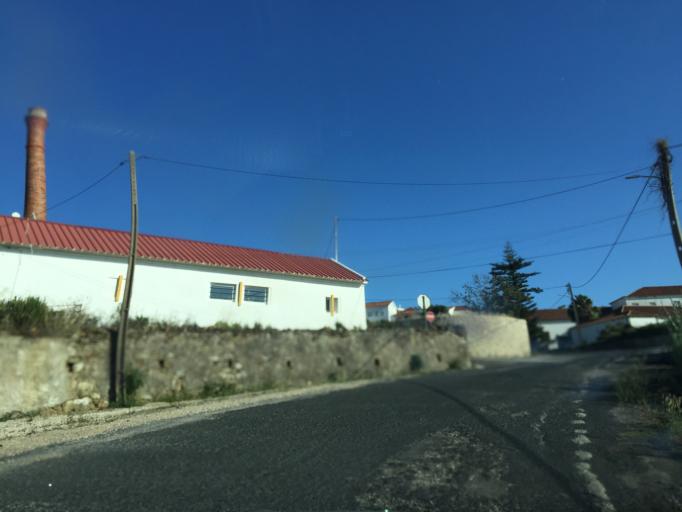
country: PT
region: Lisbon
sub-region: Torres Vedras
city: Torres Vedras
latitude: 39.0921
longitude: -9.2795
